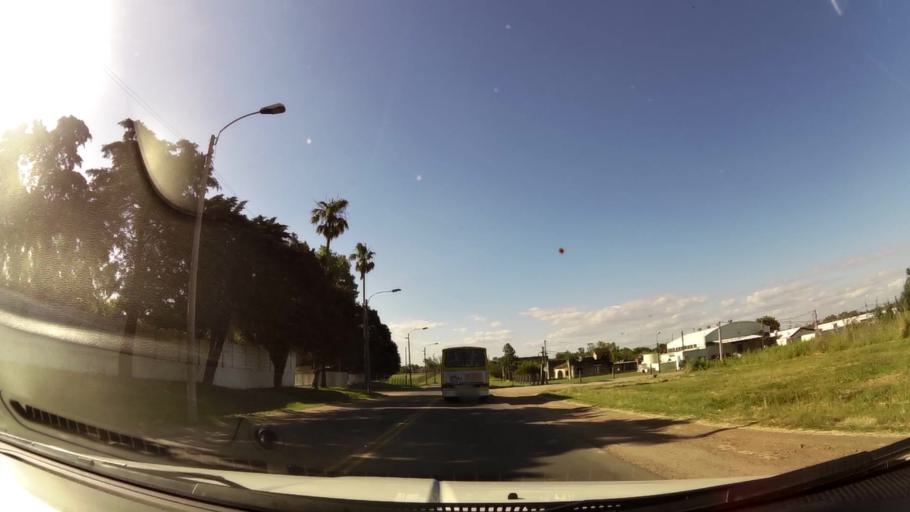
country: UY
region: Canelones
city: La Paz
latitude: -34.8117
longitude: -56.1593
